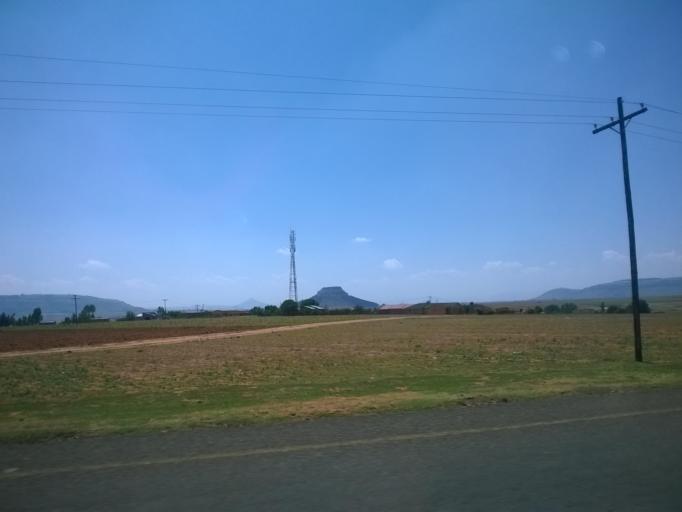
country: LS
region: Leribe
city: Maputsoe
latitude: -28.9697
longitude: 27.9688
